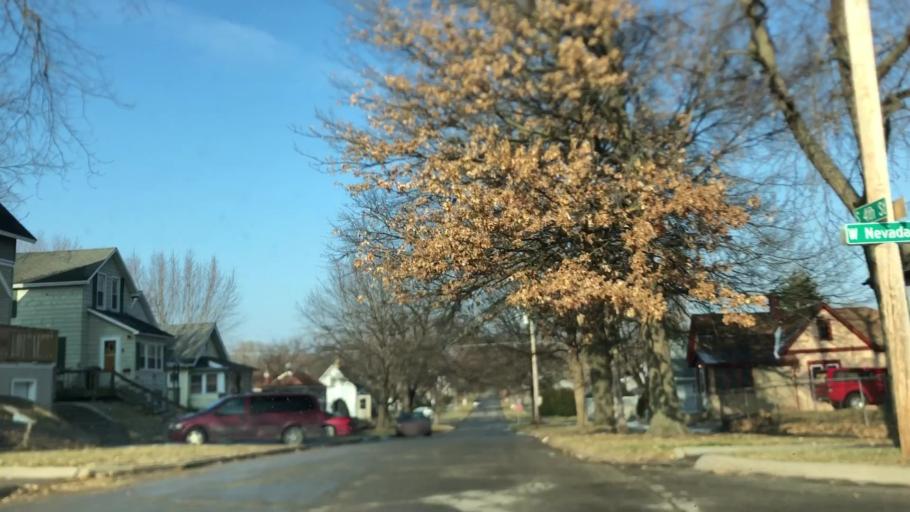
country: US
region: Iowa
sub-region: Marshall County
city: Marshalltown
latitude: 42.0442
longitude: -92.9193
